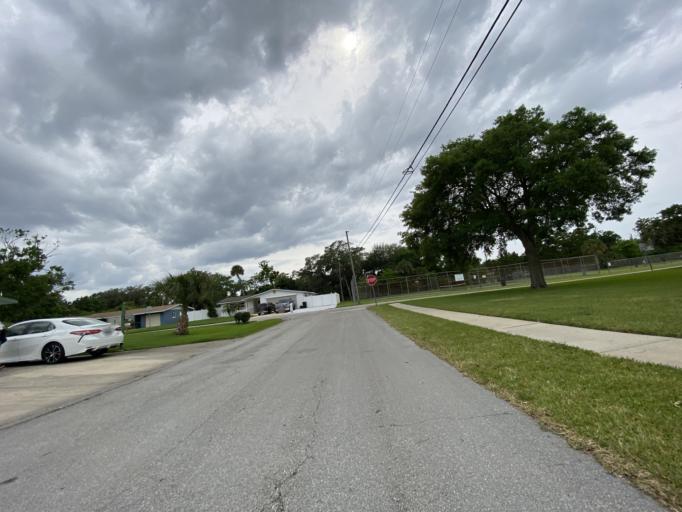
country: US
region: Florida
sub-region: Volusia County
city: South Daytona
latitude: 29.1666
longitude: -81.0099
